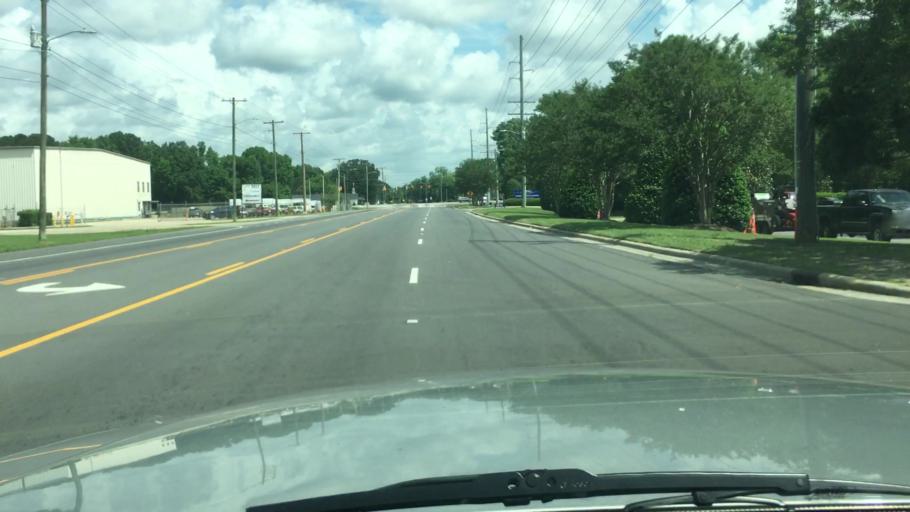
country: US
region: North Carolina
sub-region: Cumberland County
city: Fayetteville
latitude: 35.0326
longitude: -78.8725
